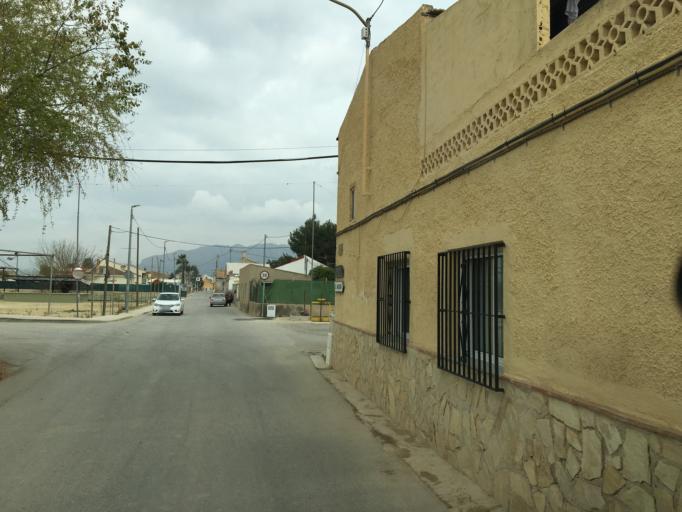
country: ES
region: Murcia
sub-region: Murcia
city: Beniel
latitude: 38.0363
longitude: -0.9863
